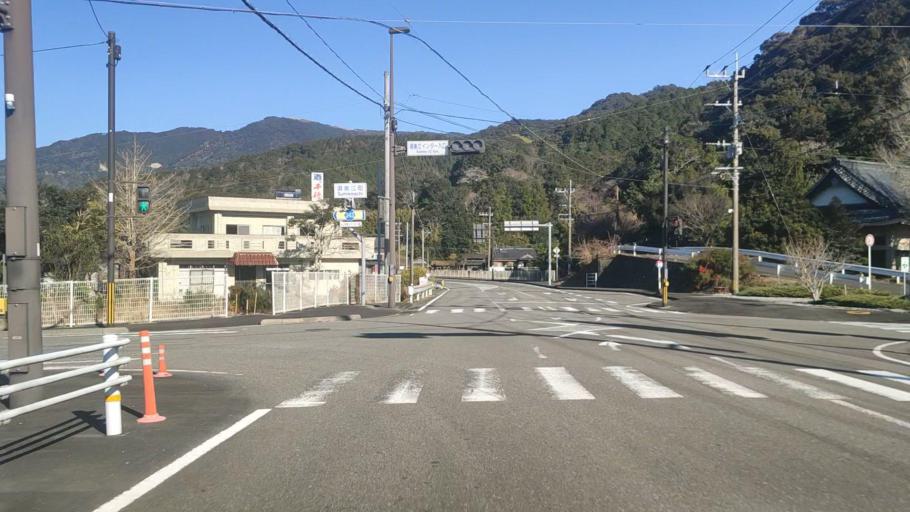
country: JP
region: Miyazaki
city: Nobeoka
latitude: 32.6654
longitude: 131.7667
